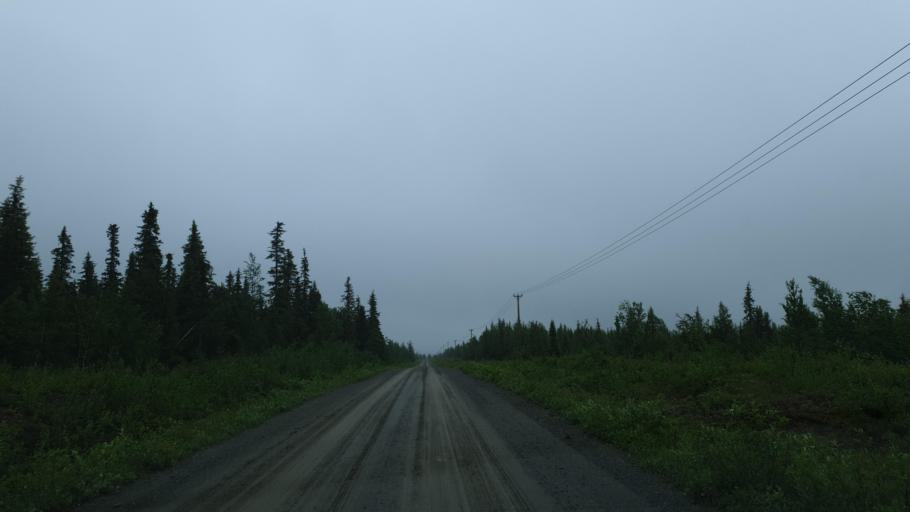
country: SE
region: Vaesterbotten
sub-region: Vilhelmina Kommun
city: Sjoberg
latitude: 65.3155
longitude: 15.9562
